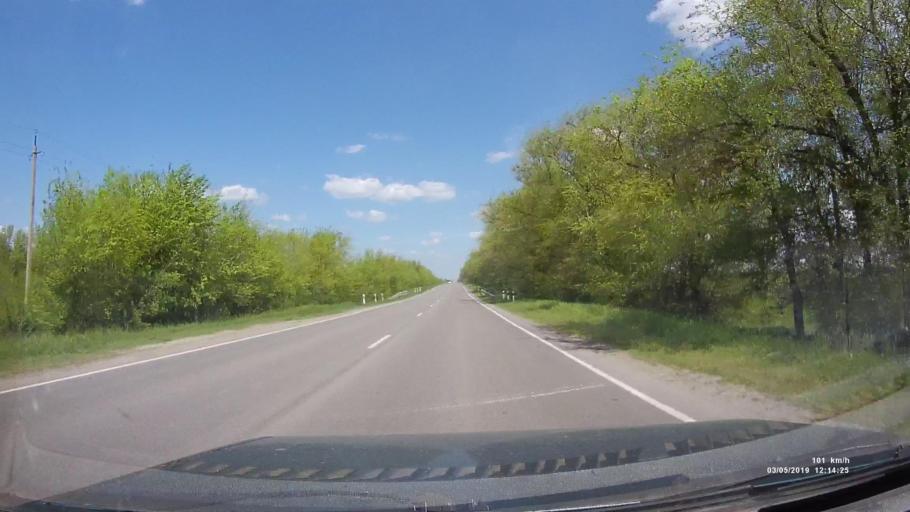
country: RU
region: Rostov
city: Melikhovskaya
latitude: 47.3438
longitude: 40.5632
